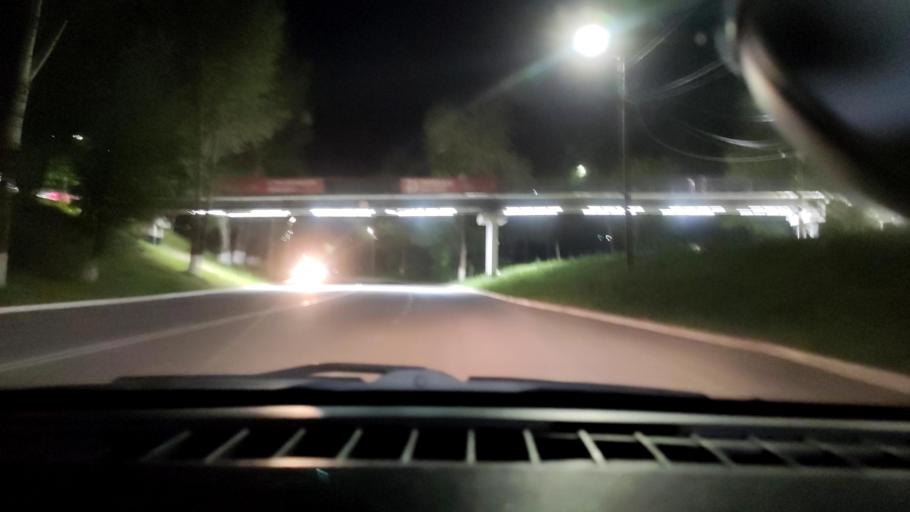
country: RU
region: Samara
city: Novokuybyshevsk
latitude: 53.0985
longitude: 49.9765
